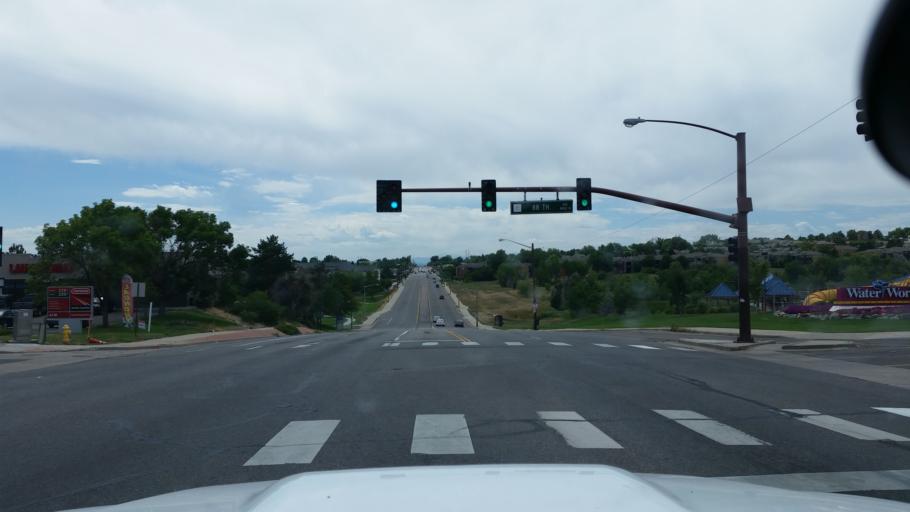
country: US
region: Colorado
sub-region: Adams County
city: Federal Heights
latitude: 39.8564
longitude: -105.0060
